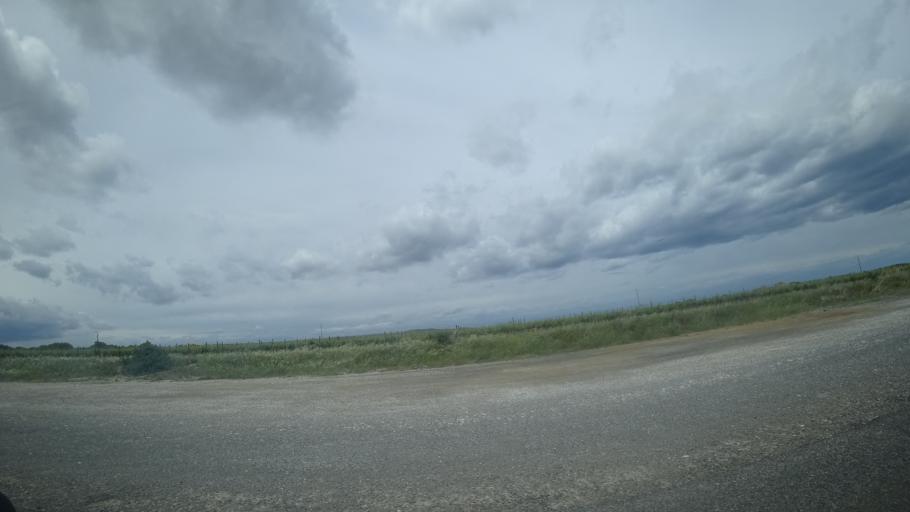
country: FR
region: Languedoc-Roussillon
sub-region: Departement de l'Aude
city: Leucate
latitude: 42.9347
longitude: 2.9994
